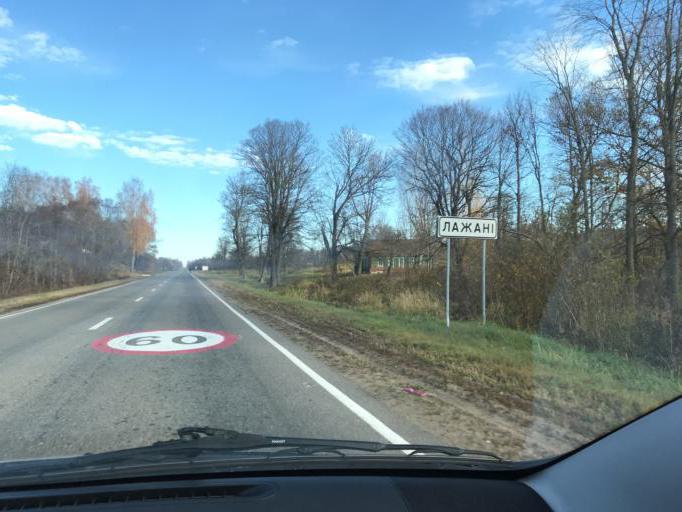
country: BY
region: Vitebsk
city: Haradok
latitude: 55.5230
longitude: 29.9718
